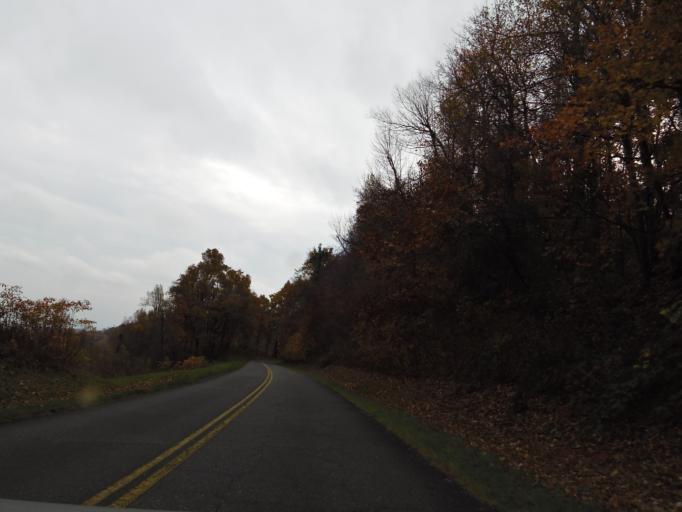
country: US
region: North Carolina
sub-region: Ashe County
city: West Jefferson
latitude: 36.2693
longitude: -81.4301
